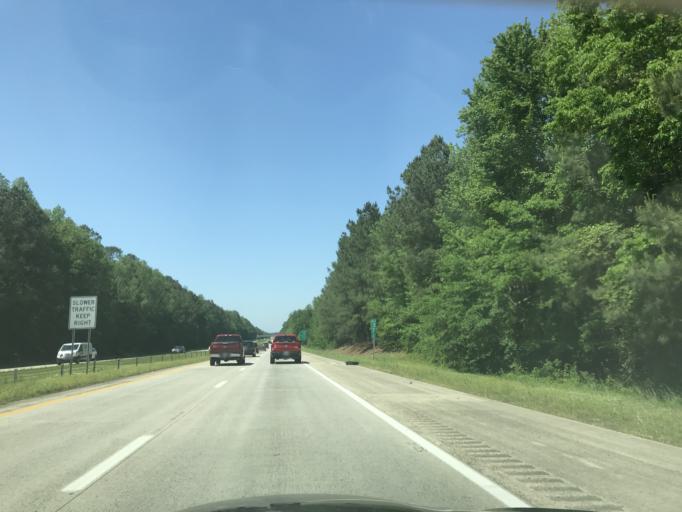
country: US
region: North Carolina
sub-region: Johnston County
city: Benson
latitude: 35.4823
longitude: -78.5509
